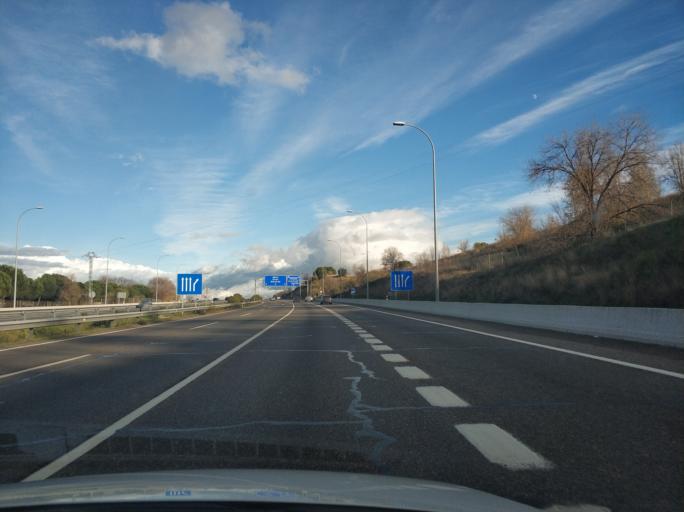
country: ES
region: Madrid
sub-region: Provincia de Madrid
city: San Sebastian de los Reyes
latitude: 40.5315
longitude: -3.6253
